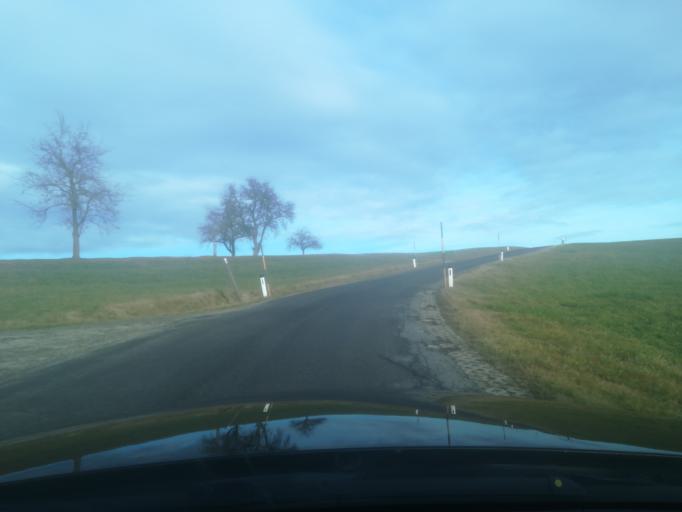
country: AT
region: Upper Austria
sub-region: Politischer Bezirk Perg
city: Perg
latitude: 48.3583
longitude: 14.6249
